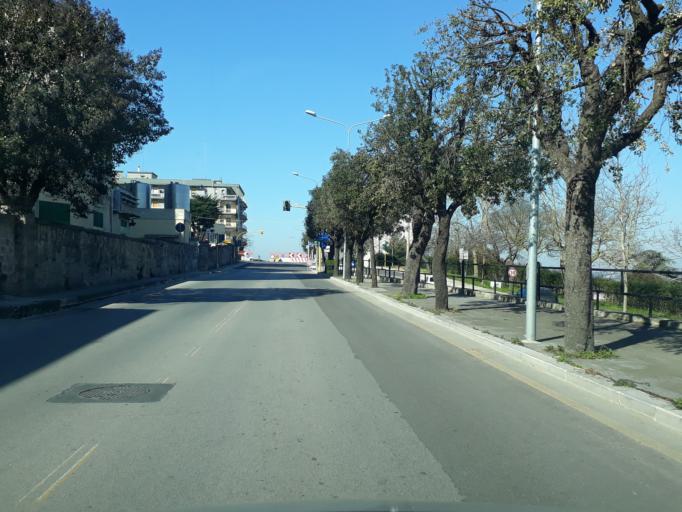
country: IT
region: Apulia
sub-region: Provincia di Taranto
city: Martina Franca
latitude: 40.7057
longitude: 17.3449
